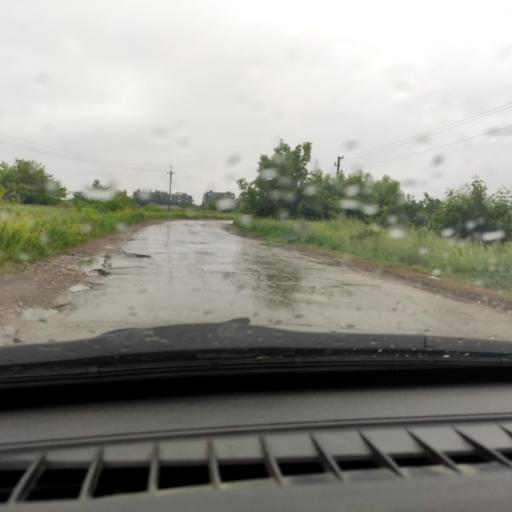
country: RU
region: Samara
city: Tol'yatti
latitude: 53.5666
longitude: 49.3572
